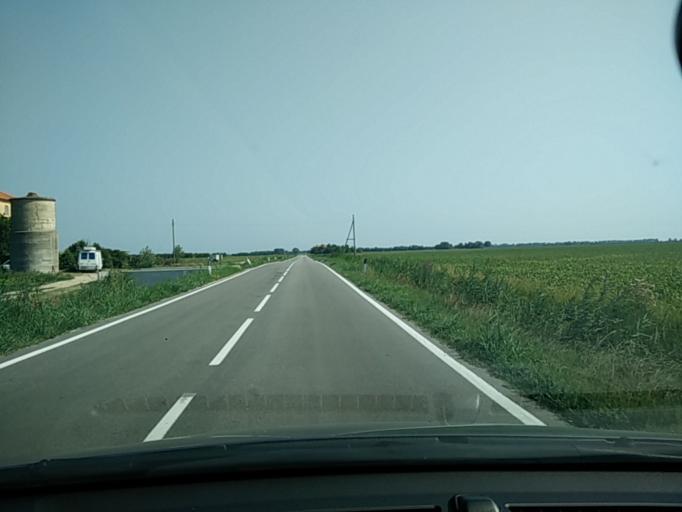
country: IT
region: Veneto
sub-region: Provincia di Venezia
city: La Salute di Livenza
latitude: 45.6414
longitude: 12.8267
